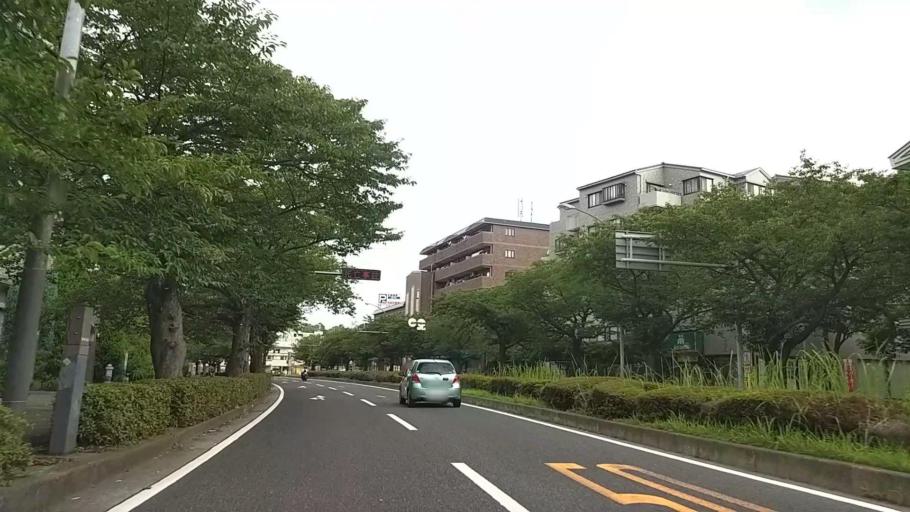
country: JP
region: Kanagawa
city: Yokohama
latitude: 35.4283
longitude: 139.6651
